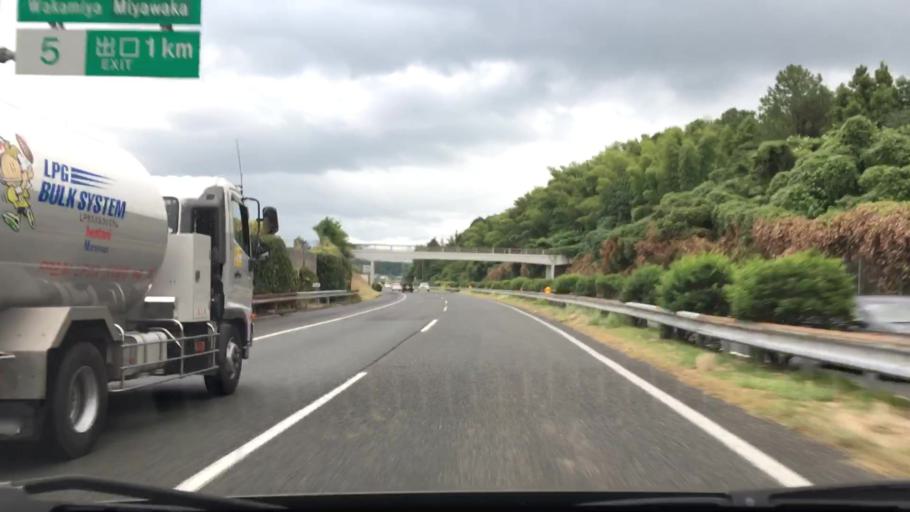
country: JP
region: Fukuoka
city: Miyata
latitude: 33.7465
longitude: 130.5967
